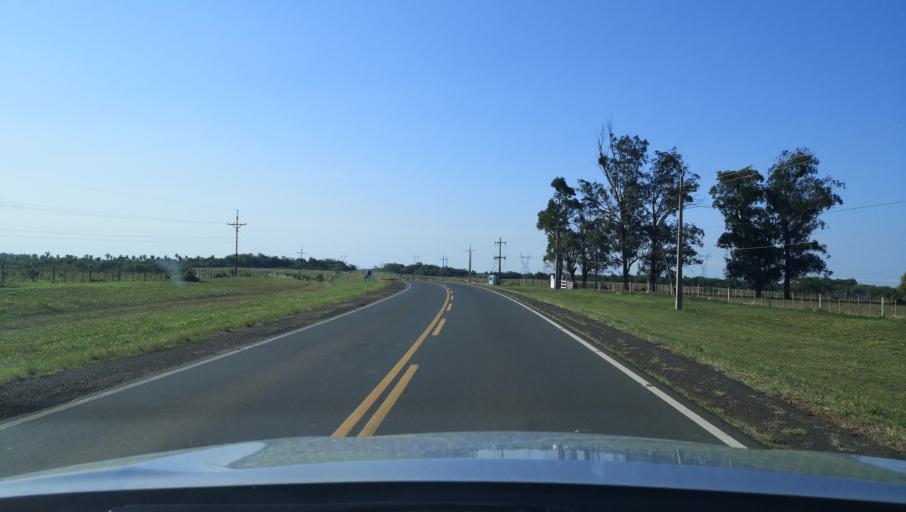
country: PY
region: Misiones
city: Santa Maria
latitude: -26.8063
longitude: -57.0201
